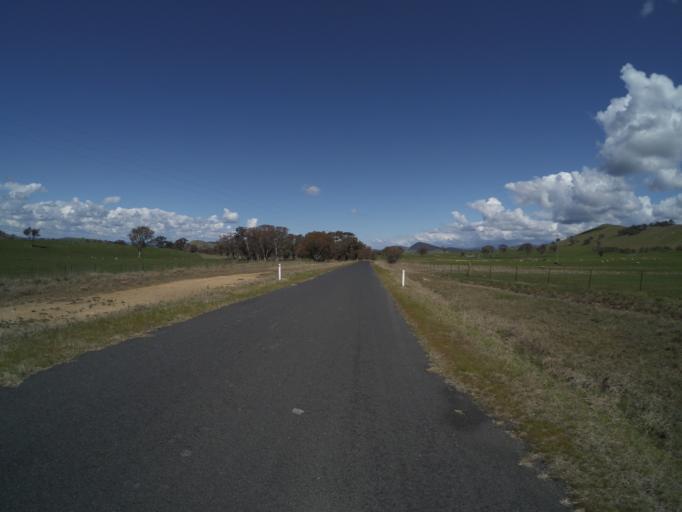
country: AU
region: New South Wales
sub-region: Yass Valley
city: Murrumbateman
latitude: -35.0967
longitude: 148.8535
